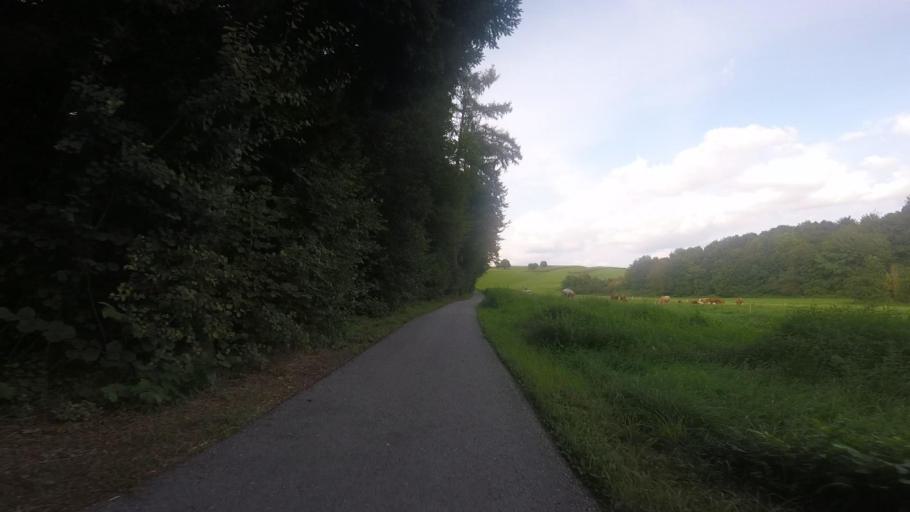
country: DE
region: Baden-Wuerttemberg
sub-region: Regierungsbezirk Stuttgart
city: Aspach
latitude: 48.9817
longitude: 9.3954
